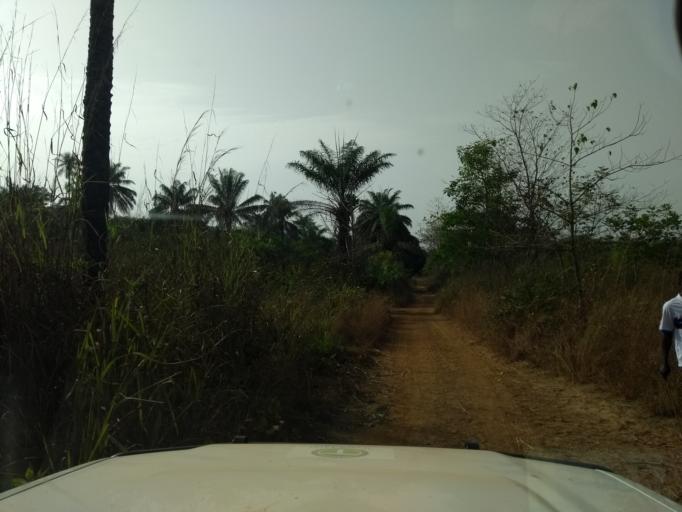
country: GN
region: Kindia
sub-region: Prefecture de Dubreka
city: Dubreka
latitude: 9.8385
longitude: -13.5597
